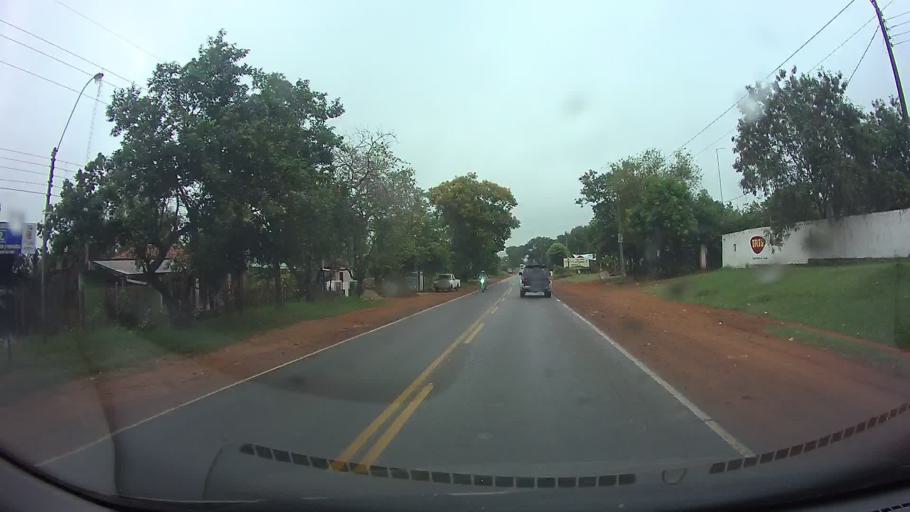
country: PY
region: Central
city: Itaugua
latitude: -25.4221
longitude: -57.3631
